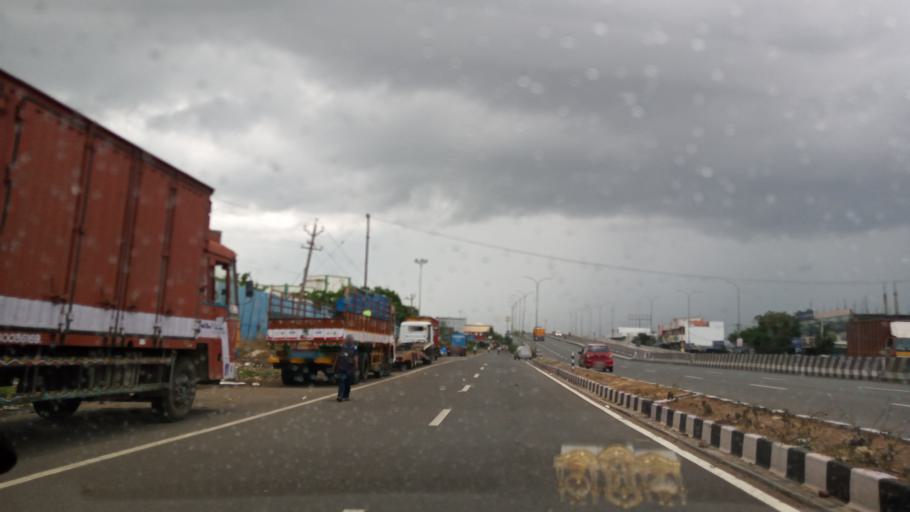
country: IN
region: Tamil Nadu
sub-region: Kancheepuram
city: Madambakkam
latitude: 12.8497
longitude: 79.9403
